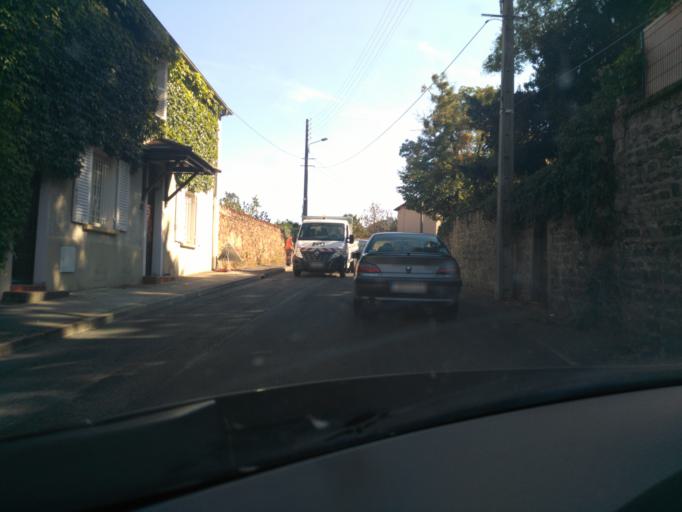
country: FR
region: Rhone-Alpes
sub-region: Departement du Rhone
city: Tarare
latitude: 45.8926
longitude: 4.4343
